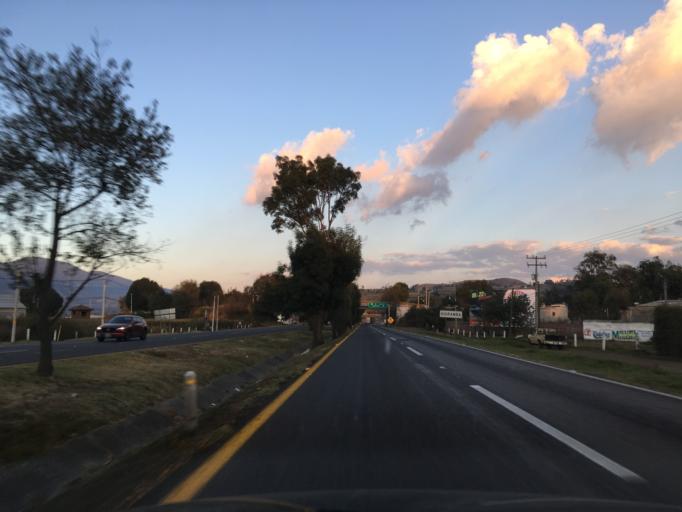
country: MX
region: Michoacan
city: Huiramba
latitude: 19.5467
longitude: -101.4432
